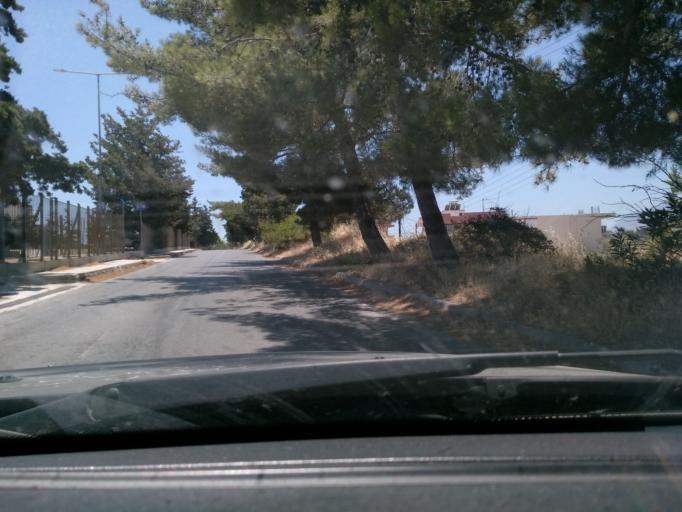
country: GR
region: Crete
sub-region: Nomos Irakleiou
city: Gazi
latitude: 35.3184
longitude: 25.1012
